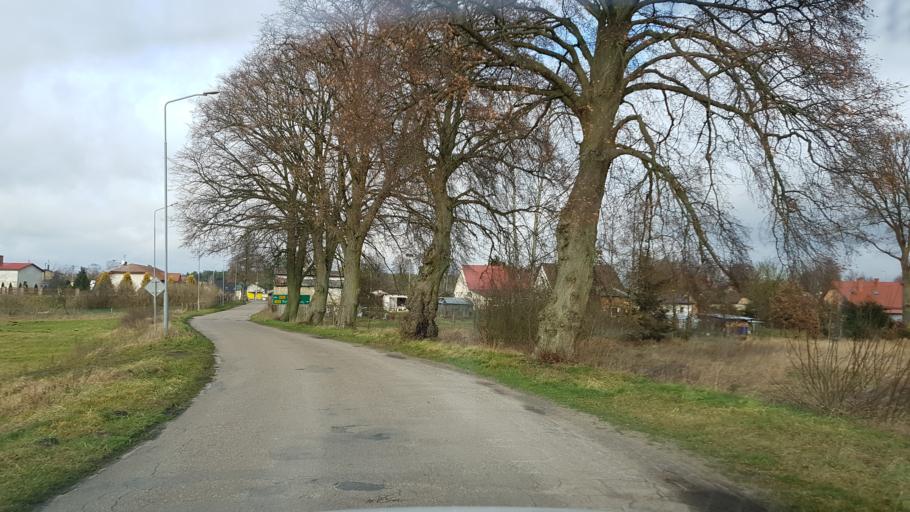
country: PL
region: West Pomeranian Voivodeship
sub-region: Powiat swidwinski
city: Rabino
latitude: 53.7731
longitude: 15.9691
